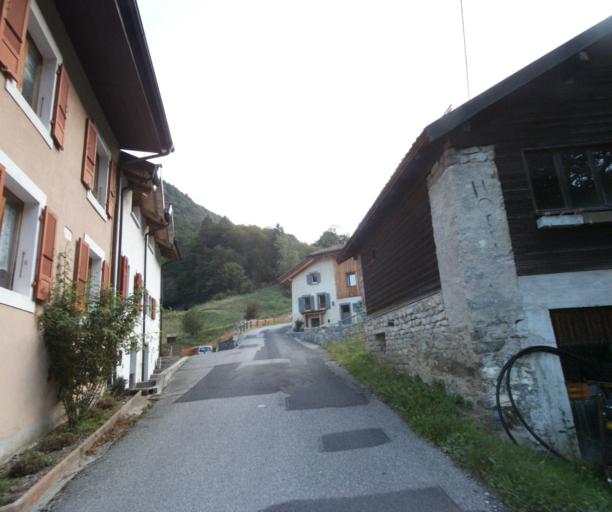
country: CH
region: Vaud
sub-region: Aigle District
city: Villeneuve
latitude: 46.4055
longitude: 6.9490
